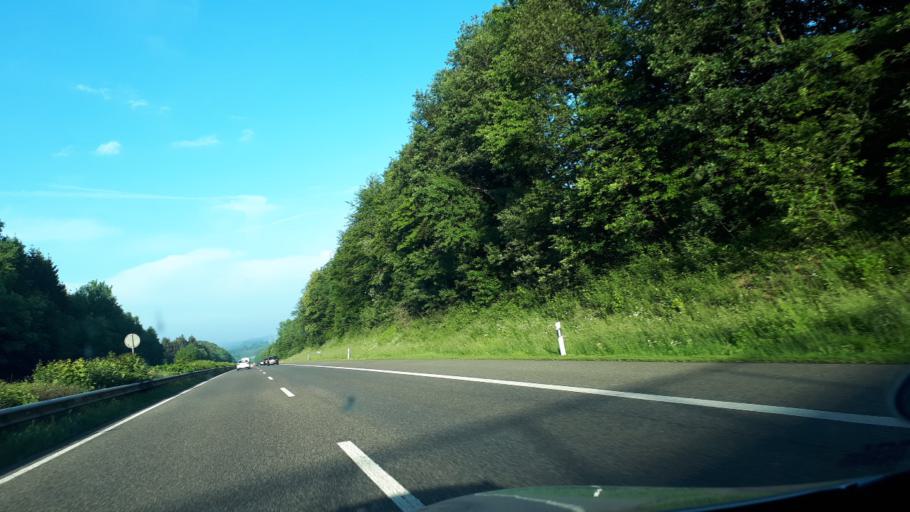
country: DE
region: Rheinland-Pfalz
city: Kaperich
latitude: 50.2363
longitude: 7.0267
